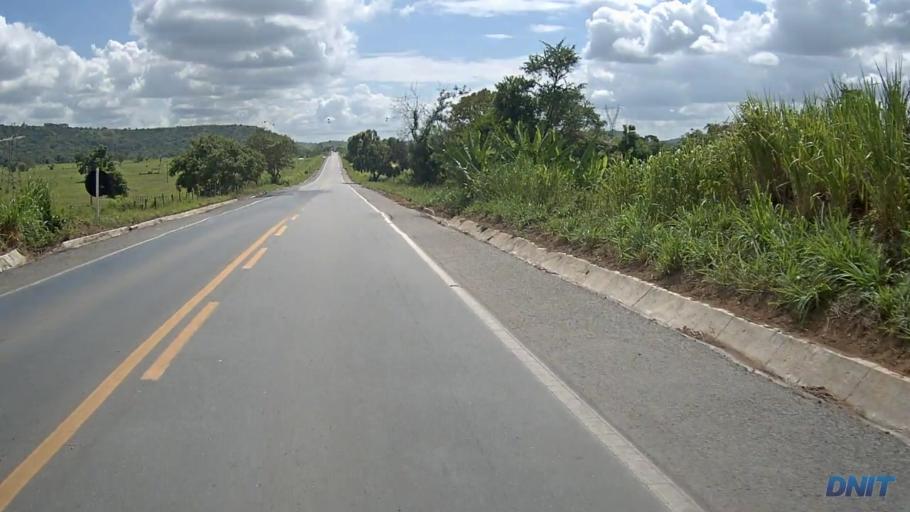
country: BR
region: Minas Gerais
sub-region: Governador Valadares
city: Governador Valadares
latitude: -19.0106
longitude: -42.1375
